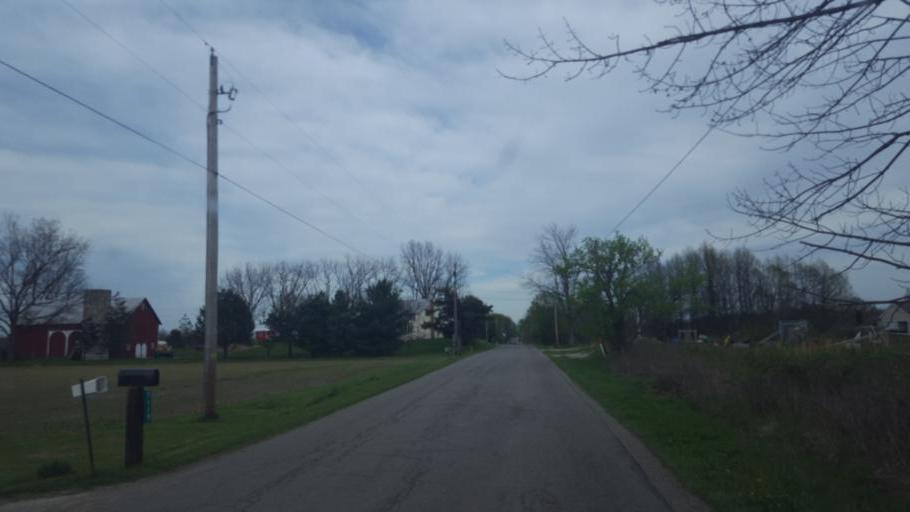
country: US
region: Ohio
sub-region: Richland County
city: Lexington
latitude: 40.6812
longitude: -82.6705
